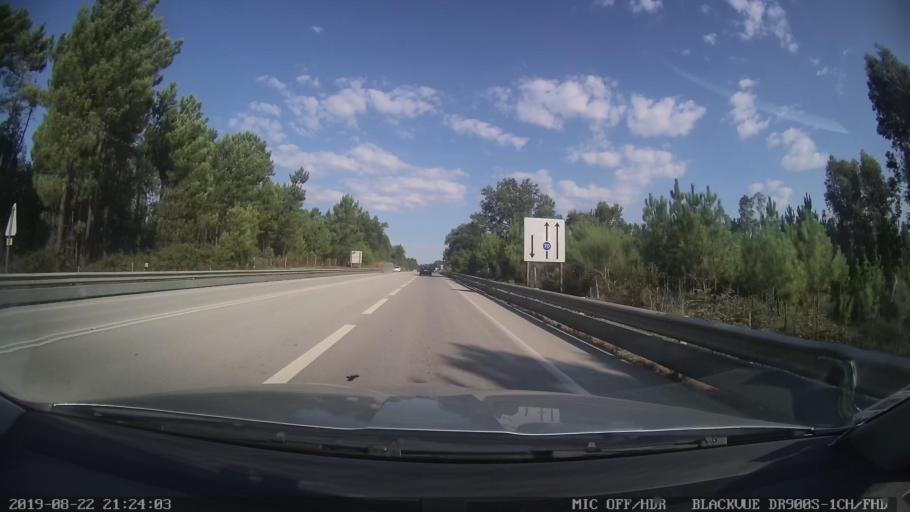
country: PT
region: Castelo Branco
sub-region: Serta
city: Serta
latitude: 39.8376
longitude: -8.1164
